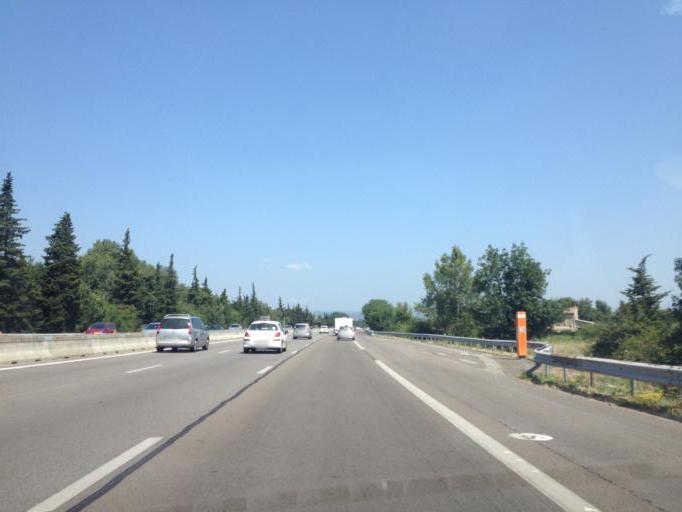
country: FR
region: Rhone-Alpes
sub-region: Departement de la Drome
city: Saulce-sur-Rhone
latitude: 44.6923
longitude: 4.7905
